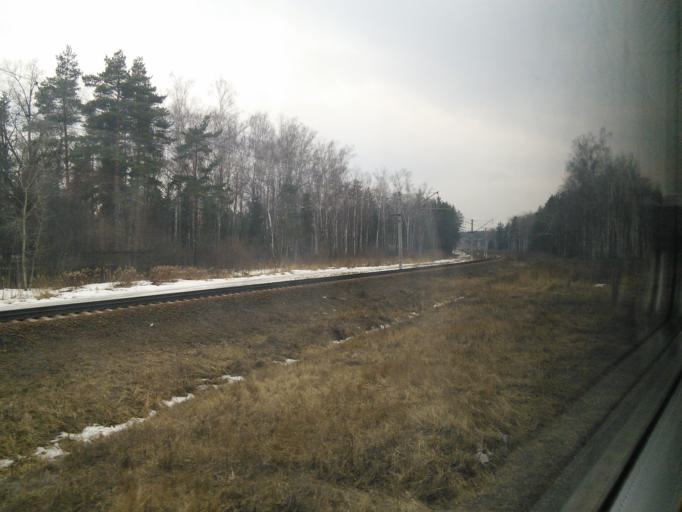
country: RU
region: Moskovskaya
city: Vostryakovo
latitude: 55.4174
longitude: 37.8081
